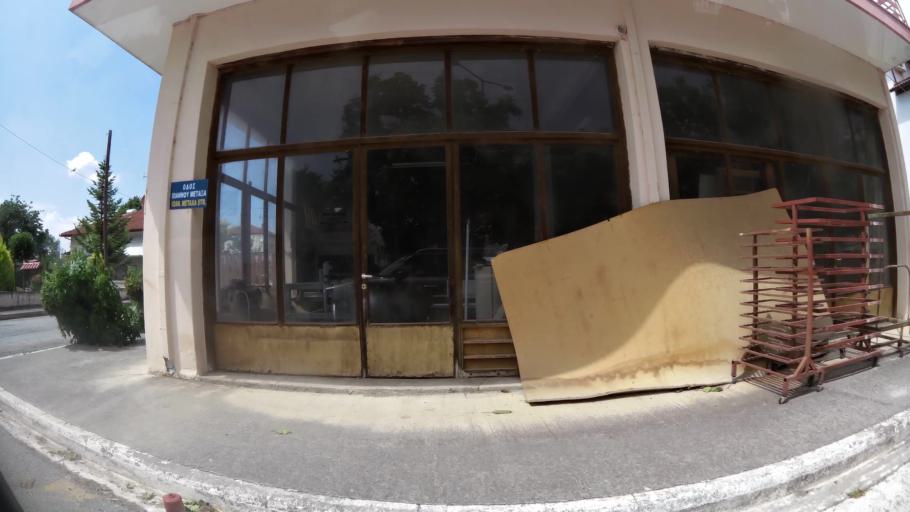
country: GR
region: Central Macedonia
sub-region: Nomos Pierias
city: Korinos
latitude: 40.3130
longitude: 22.5878
